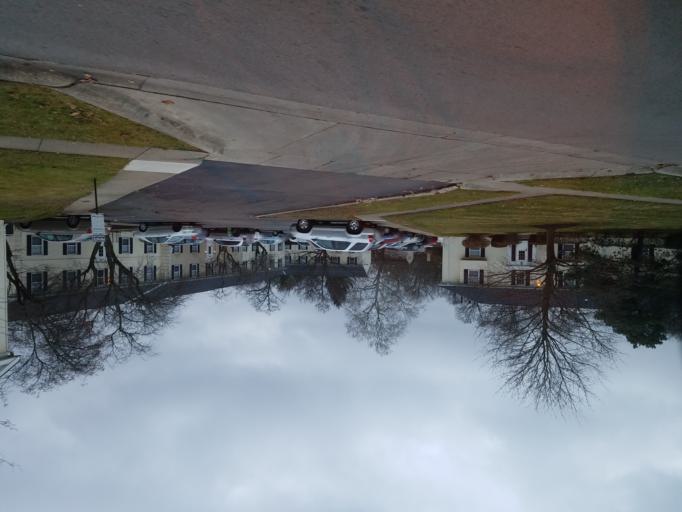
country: US
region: Ohio
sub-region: Franklin County
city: Minerva Park
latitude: 40.0777
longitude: -82.9651
